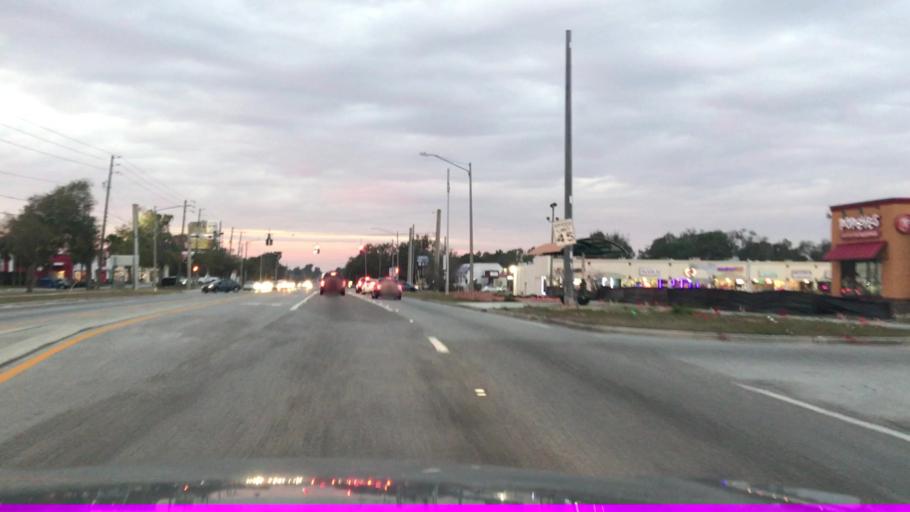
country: US
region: Florida
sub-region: Orange County
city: Pine Hills
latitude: 28.5790
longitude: -81.4761
